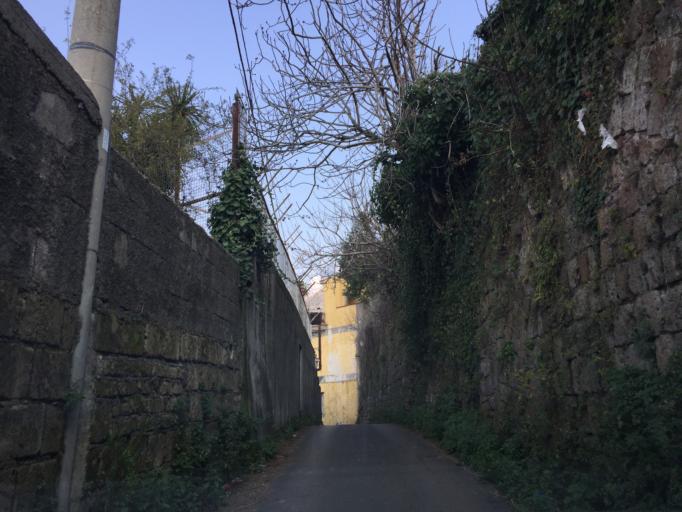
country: IT
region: Campania
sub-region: Provincia di Napoli
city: Castellammare di Stabia
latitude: 40.6867
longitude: 14.4863
